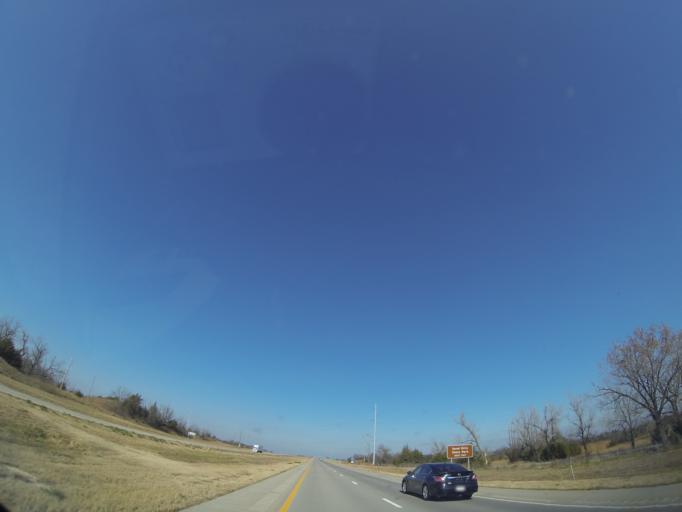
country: US
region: Kansas
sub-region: Reno County
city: Hutchinson
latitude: 38.1076
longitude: -97.8754
